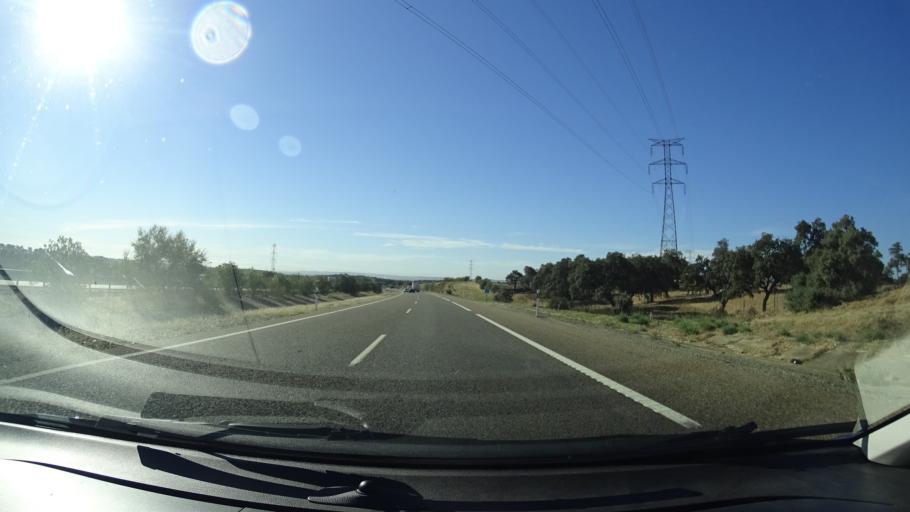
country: ES
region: Andalusia
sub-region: Provincia de Sevilla
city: Gerena
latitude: 37.5922
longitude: -6.1239
